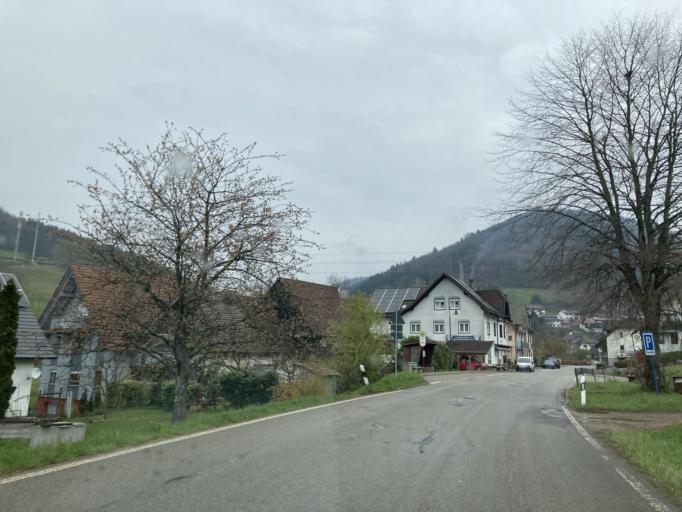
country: DE
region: Baden-Wuerttemberg
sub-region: Freiburg Region
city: Muhlenbach
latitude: 48.2128
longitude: 8.1382
